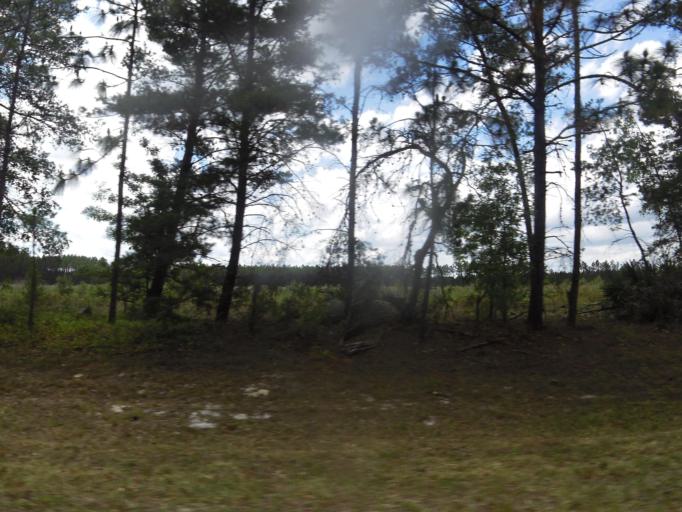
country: US
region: Florida
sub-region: Clay County
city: Green Cove Springs
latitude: 29.9405
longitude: -81.7462
